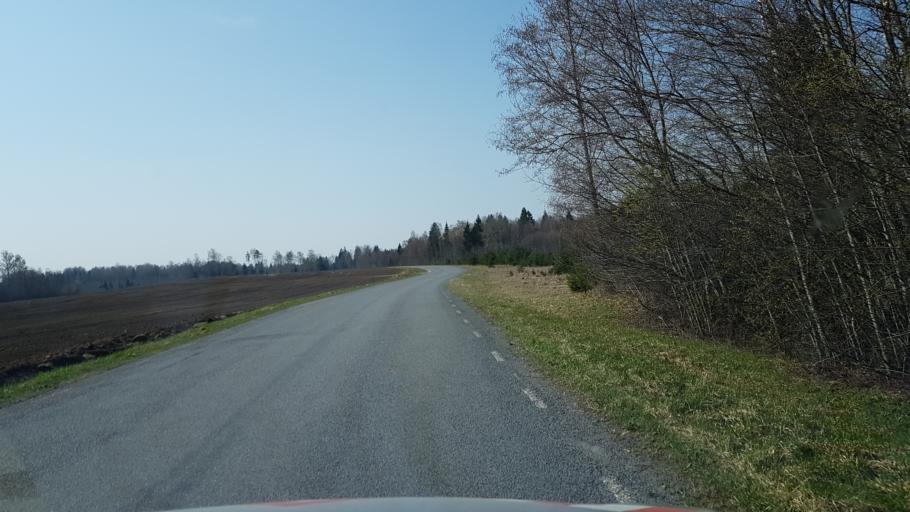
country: EE
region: Raplamaa
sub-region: Maerjamaa vald
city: Marjamaa
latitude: 58.8776
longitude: 24.3802
